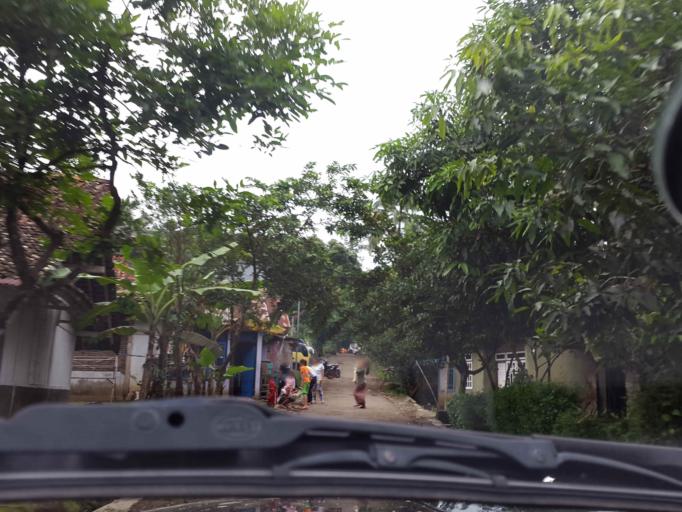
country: ID
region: Central Java
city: Wonosobo
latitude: -7.4394
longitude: 109.8610
